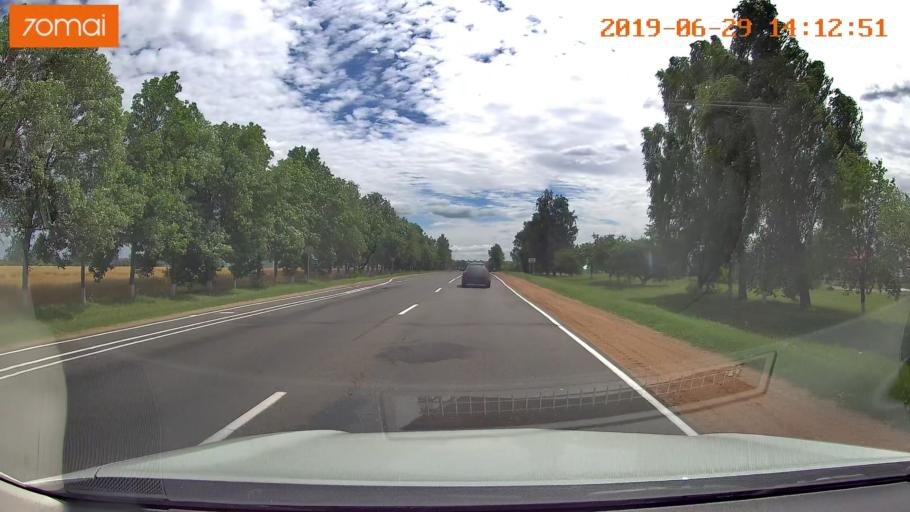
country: BY
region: Minsk
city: Salihorsk
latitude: 52.8068
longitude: 27.5089
